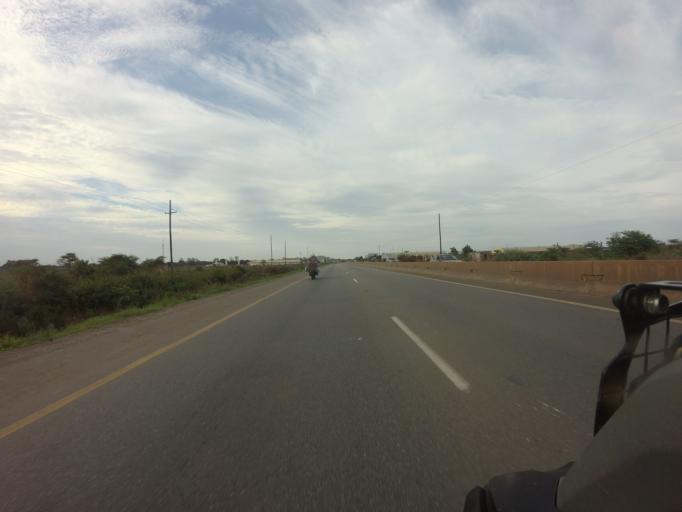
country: ZM
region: Lusaka
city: Lusaka
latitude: -15.4927
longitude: 28.2556
